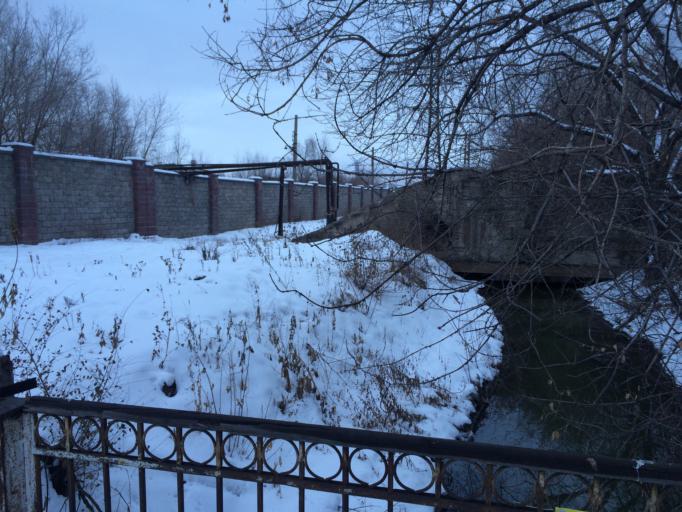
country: RU
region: Chelyabinsk
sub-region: Gorod Magnitogorsk
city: Magnitogorsk
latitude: 53.4027
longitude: 59.0456
